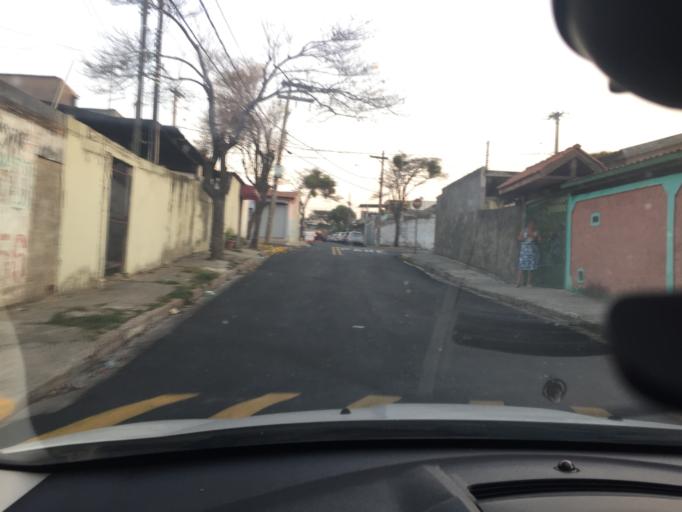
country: BR
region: Sao Paulo
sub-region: Varzea Paulista
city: Varzea Paulista
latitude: -23.2072
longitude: -46.8472
